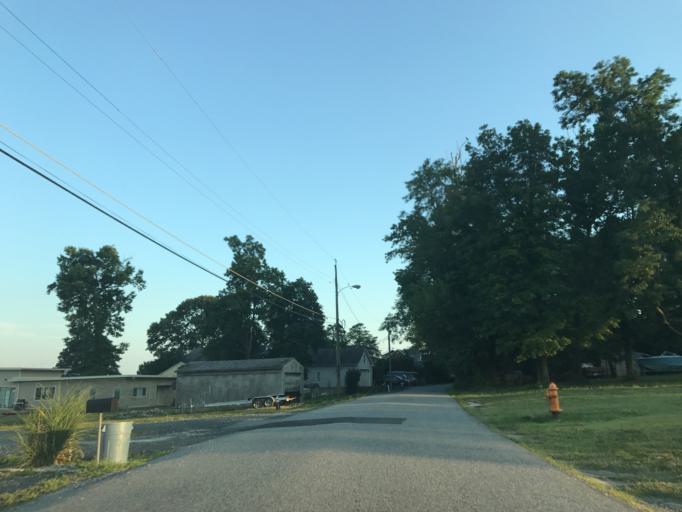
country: US
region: Maryland
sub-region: Baltimore County
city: Edgemere
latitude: 39.2681
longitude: -76.3958
